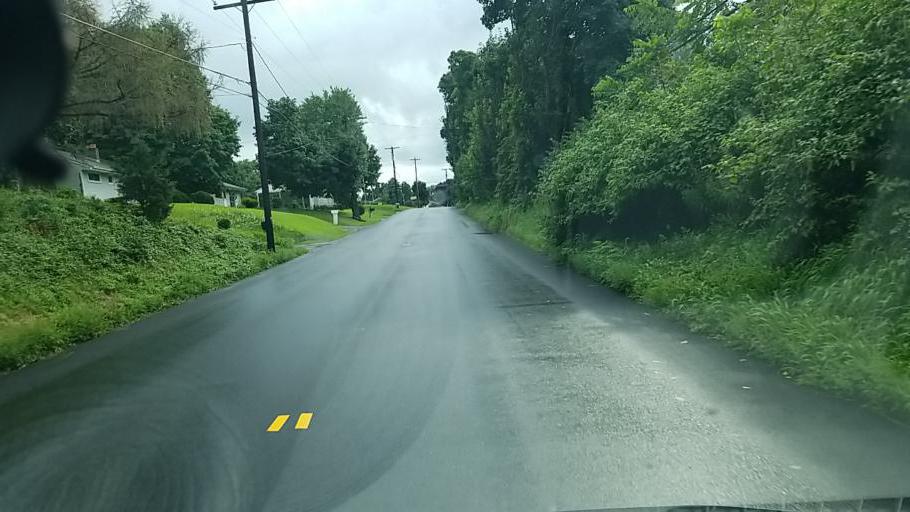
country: US
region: Pennsylvania
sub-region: Dauphin County
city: Millersburg
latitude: 40.5541
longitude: -76.9353
